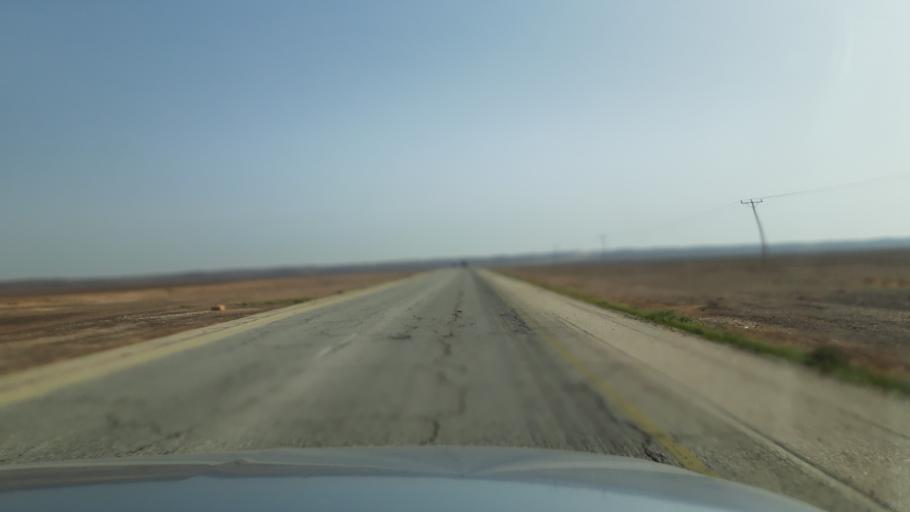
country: JO
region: Amman
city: Al Azraq ash Shamali
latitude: 31.8385
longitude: 36.6387
